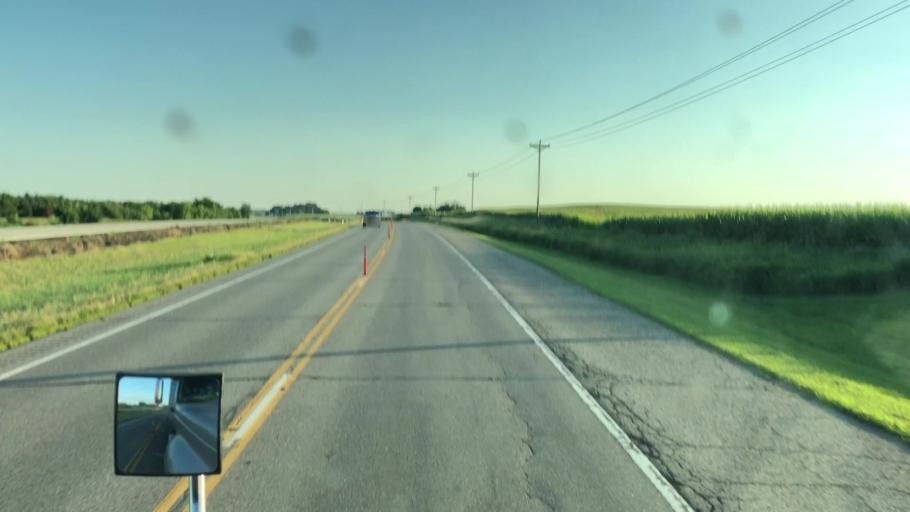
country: US
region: Minnesota
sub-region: Scott County
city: Belle Plaine
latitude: 44.5848
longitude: -93.8318
